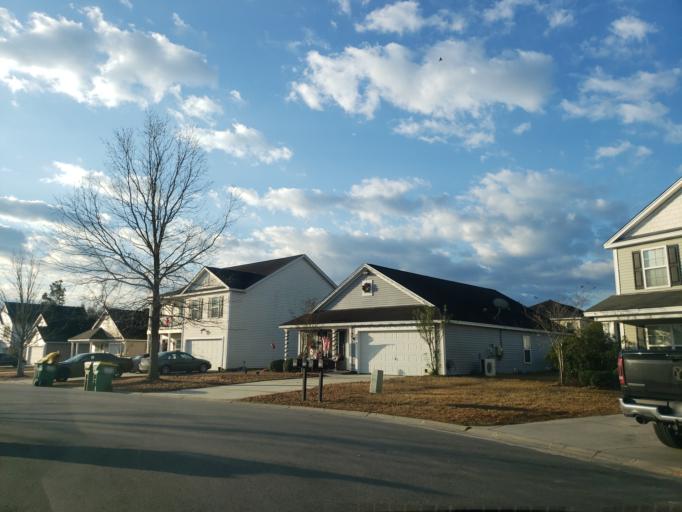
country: US
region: Georgia
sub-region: Chatham County
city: Bloomingdale
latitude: 32.1551
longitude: -81.2714
